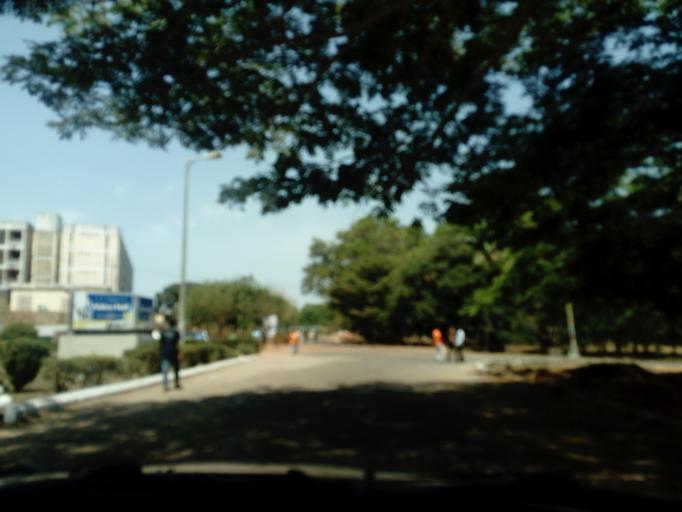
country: GH
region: Central
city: Cape Coast
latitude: 5.1154
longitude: -1.2820
